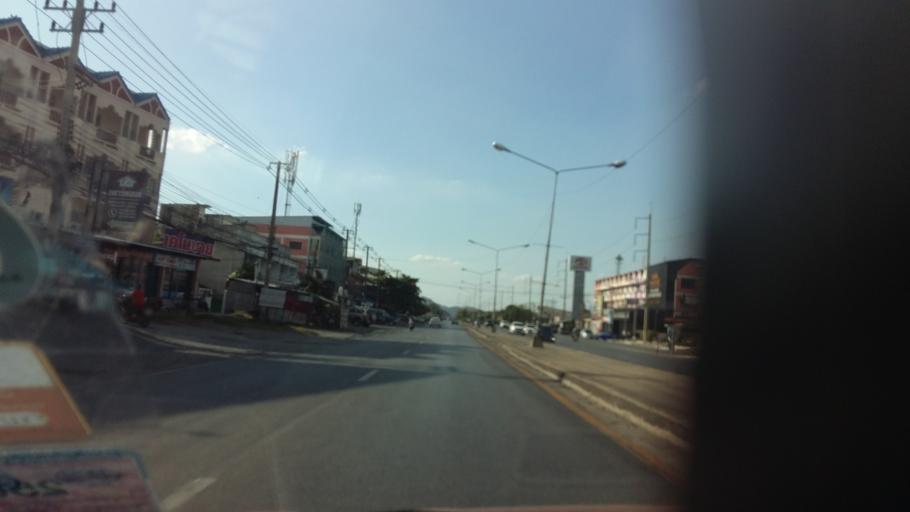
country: TH
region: Lop Buri
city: Lop Buri
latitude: 14.8272
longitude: 100.6469
